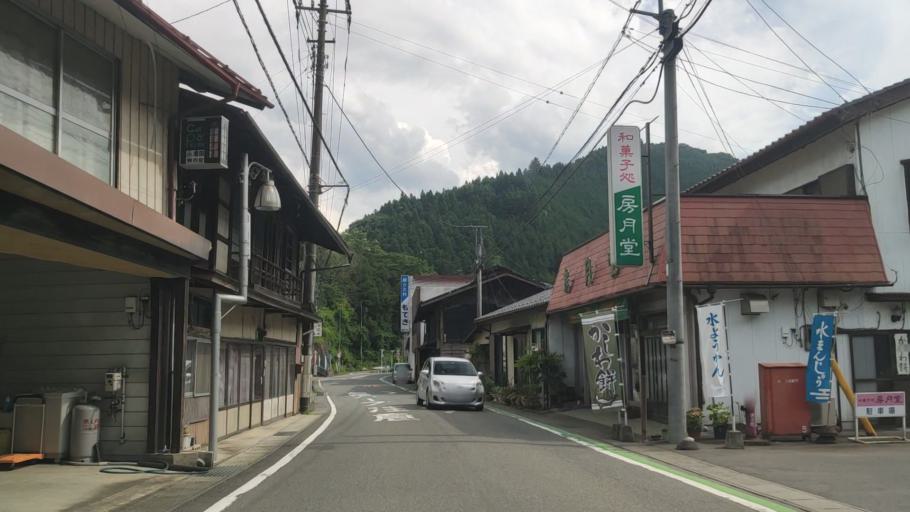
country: JP
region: Gunma
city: Tomioka
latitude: 36.1682
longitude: 138.7283
